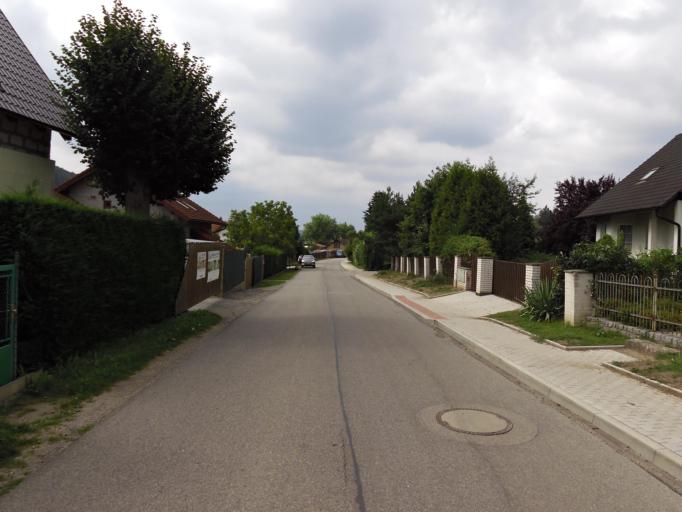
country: CZ
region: Central Bohemia
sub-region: Okres Benesov
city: Cercany
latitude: 49.8701
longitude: 14.7217
